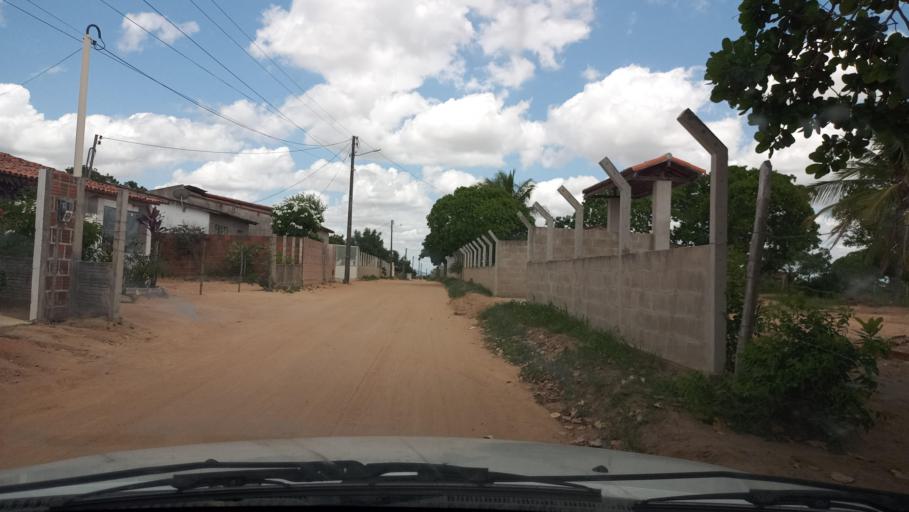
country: BR
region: Rio Grande do Norte
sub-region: Sao Jose Do Campestre
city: Sao Jose do Campestre
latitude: -6.4349
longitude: -35.6344
